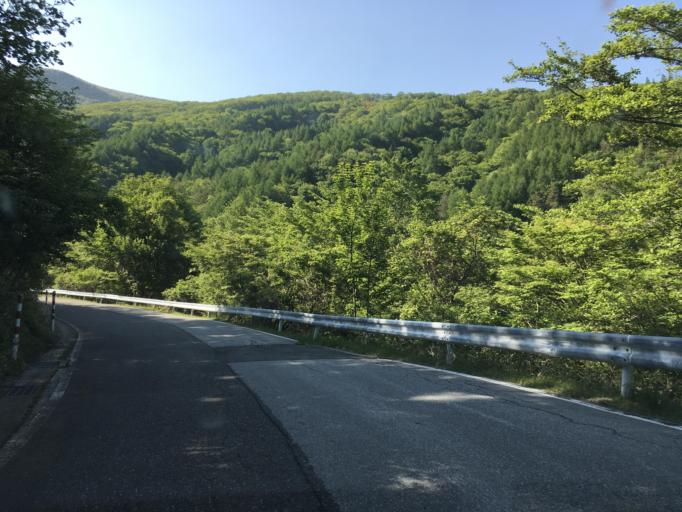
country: JP
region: Iwate
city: Ofunato
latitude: 39.1844
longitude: 141.7463
